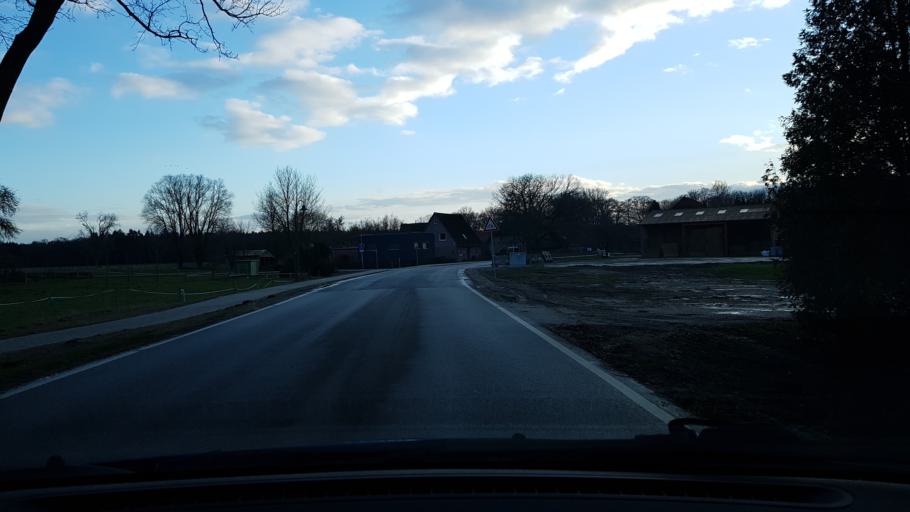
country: DE
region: Lower Saxony
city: Ludersburg
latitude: 53.3052
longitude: 10.5711
